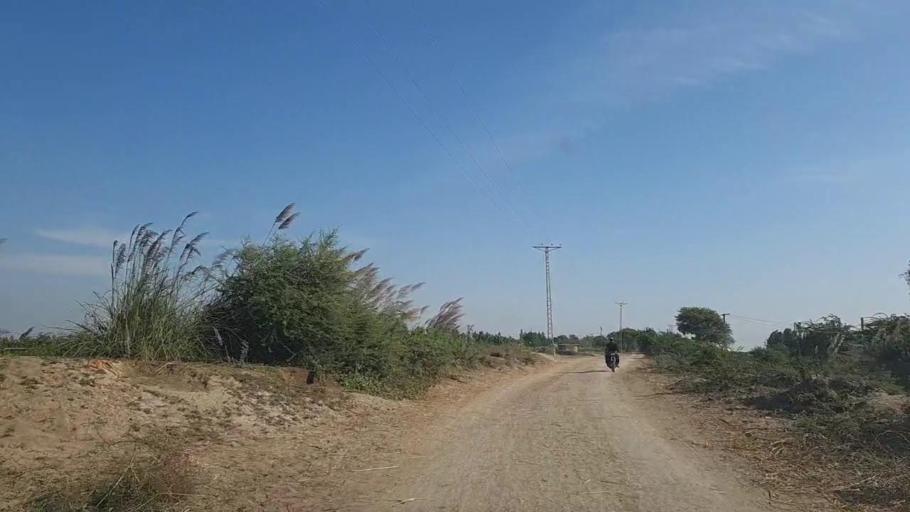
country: PK
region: Sindh
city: Bulri
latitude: 24.8127
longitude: 68.3217
